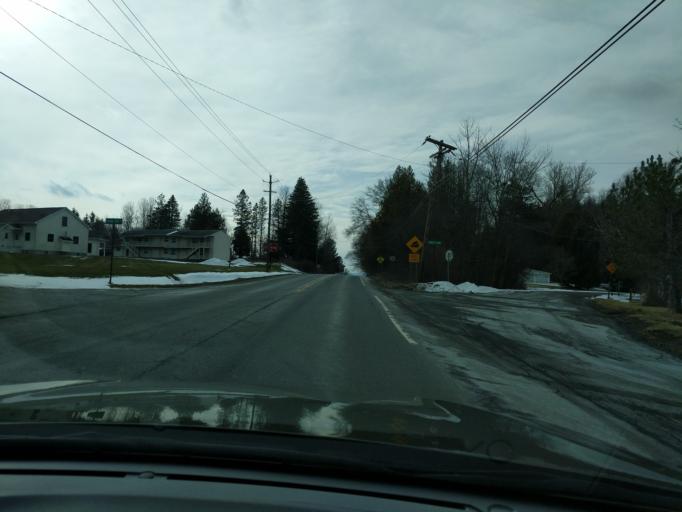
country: US
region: New York
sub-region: Tompkins County
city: Northeast Ithaca
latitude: 42.4604
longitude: -76.4273
